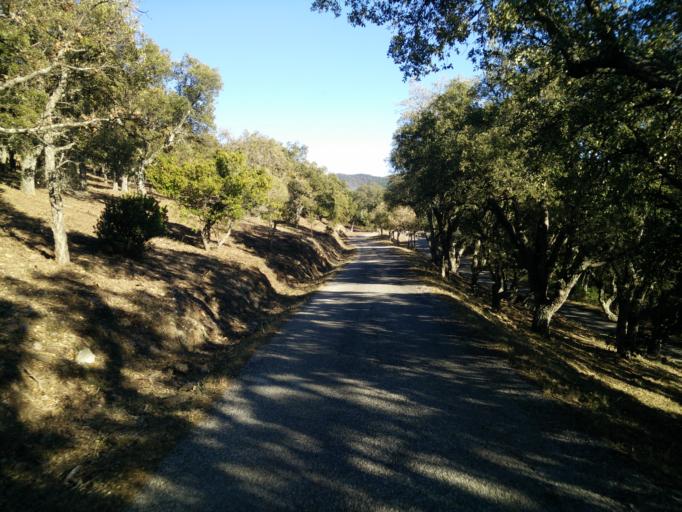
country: FR
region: Provence-Alpes-Cote d'Azur
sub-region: Departement du Var
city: Collobrieres
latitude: 43.2665
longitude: 6.2920
